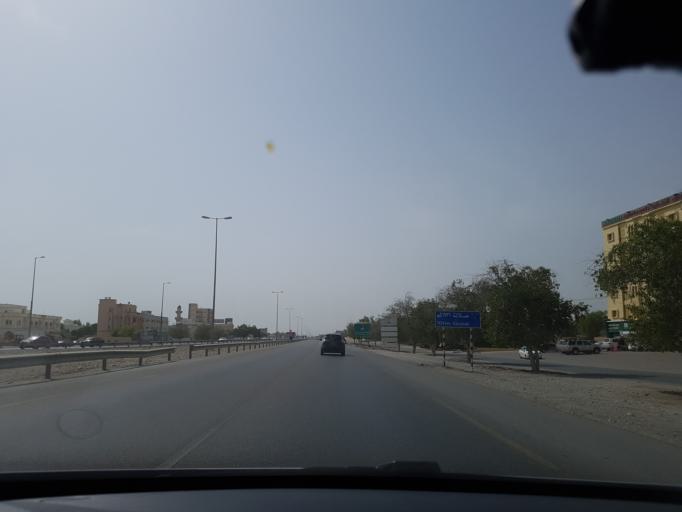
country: OM
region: Al Batinah
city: Al Khaburah
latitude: 23.9748
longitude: 57.0878
